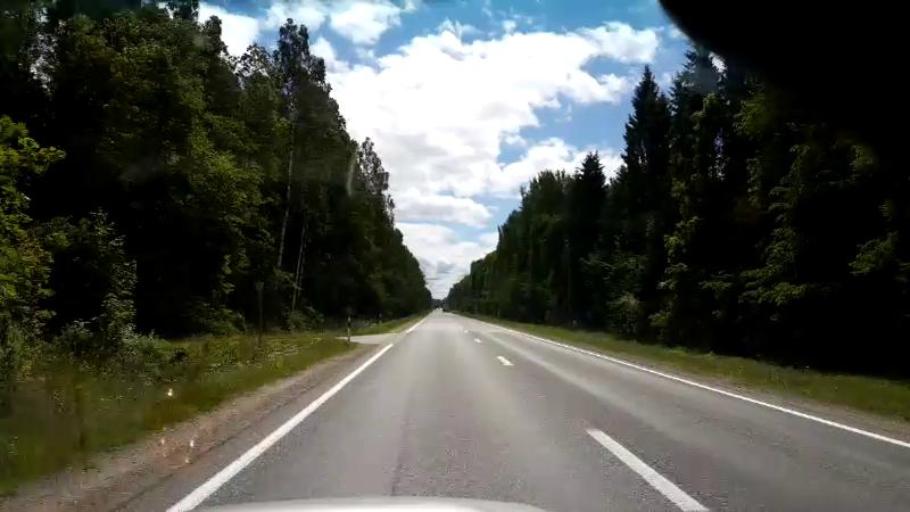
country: LV
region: Salacgrivas
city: Salacgriva
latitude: 57.5893
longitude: 24.4205
